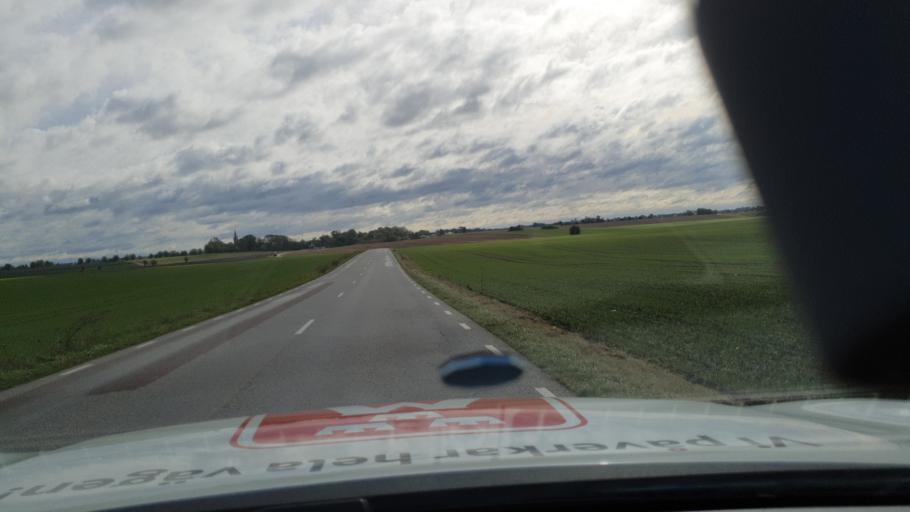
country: SE
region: Skane
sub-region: Malmo
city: Tygelsjo
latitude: 55.5122
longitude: 13.0217
